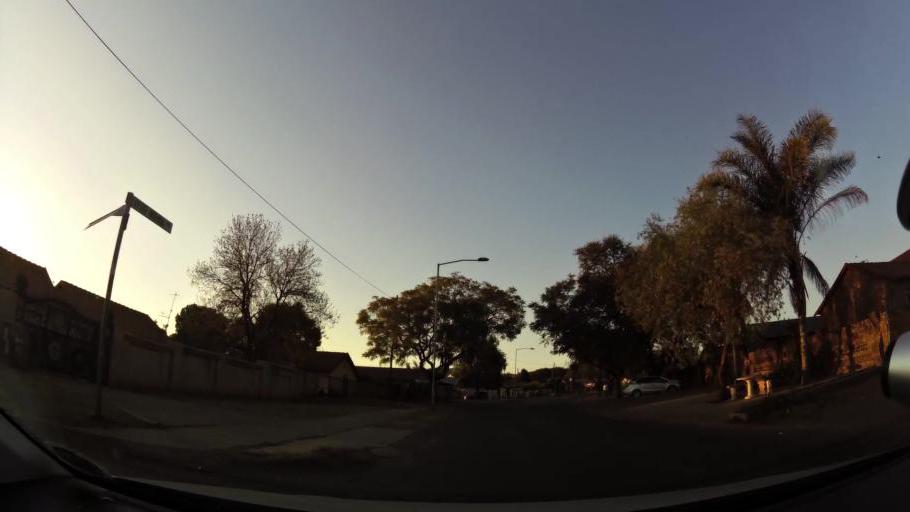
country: ZA
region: Gauteng
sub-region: City of Tshwane Metropolitan Municipality
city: Pretoria
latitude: -25.7395
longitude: 28.1379
